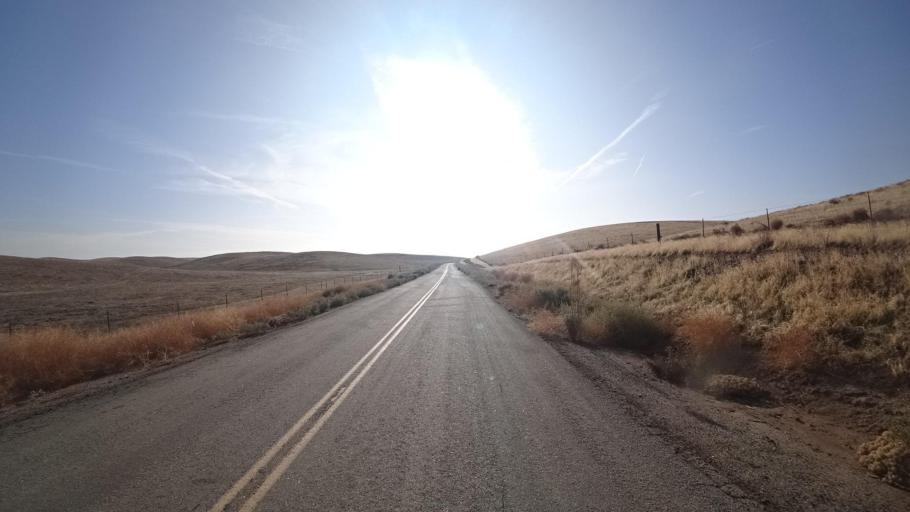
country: US
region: California
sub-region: Tulare County
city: Richgrove
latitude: 35.6339
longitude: -119.0351
